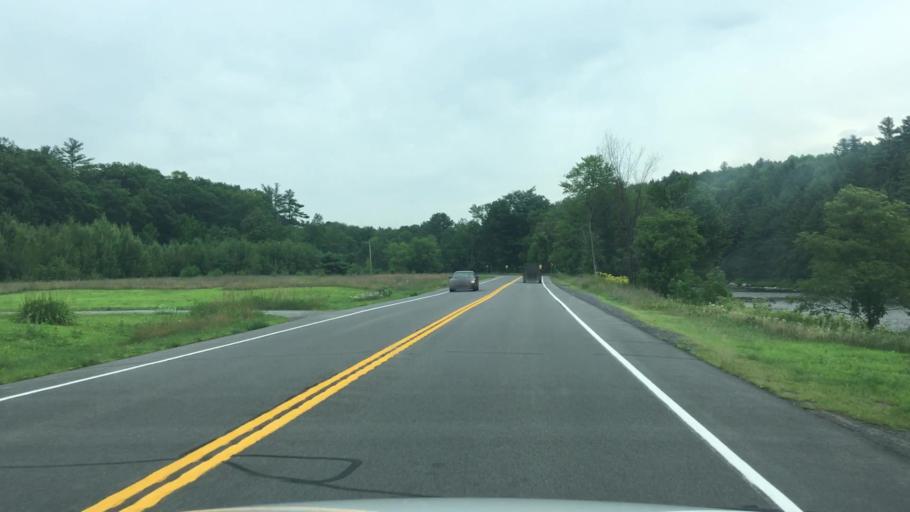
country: US
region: New York
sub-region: Clinton County
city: Peru
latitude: 44.4510
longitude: -73.6479
